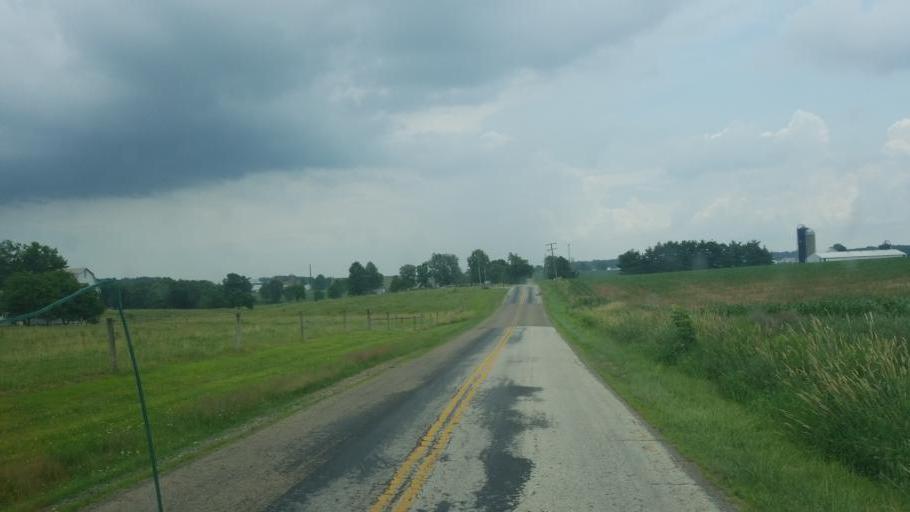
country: US
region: Ohio
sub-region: Wayne County
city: Smithville
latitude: 40.9016
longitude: -81.8777
